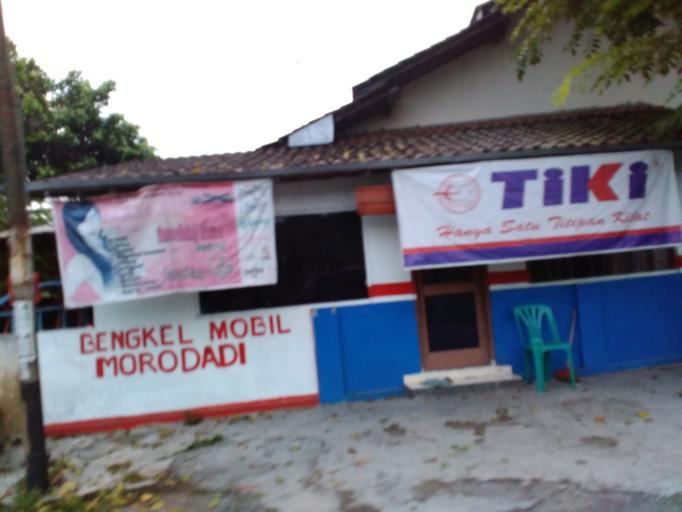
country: ID
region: Central Java
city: Boyolali
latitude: -7.5371
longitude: 110.6102
